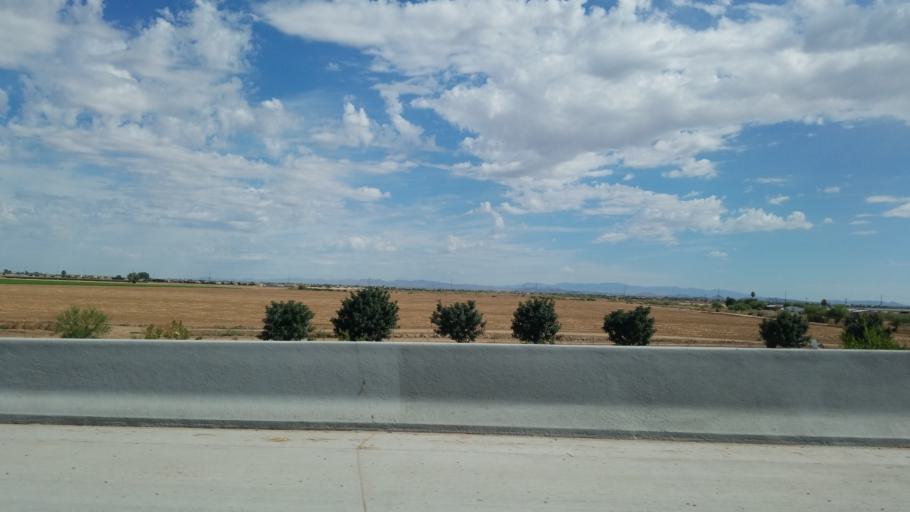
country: US
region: Arizona
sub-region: Maricopa County
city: Citrus Park
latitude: 33.5594
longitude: -112.3954
